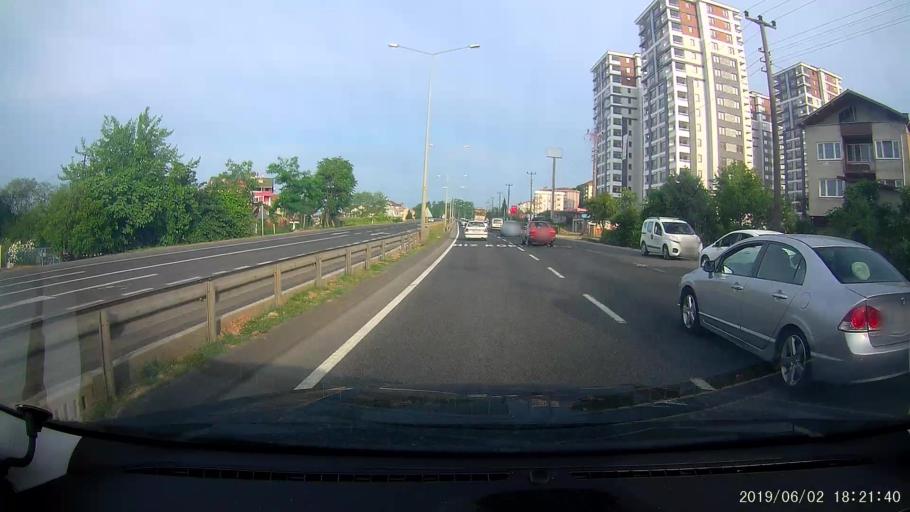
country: TR
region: Ordu
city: Fatsa
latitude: 41.0634
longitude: 37.4708
